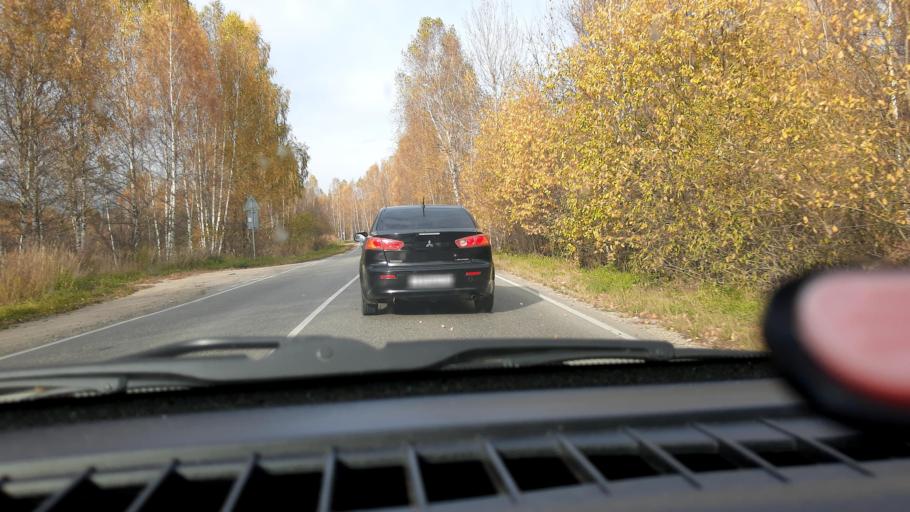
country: RU
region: Nizjnij Novgorod
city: Neklyudovo
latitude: 56.5005
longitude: 43.8509
